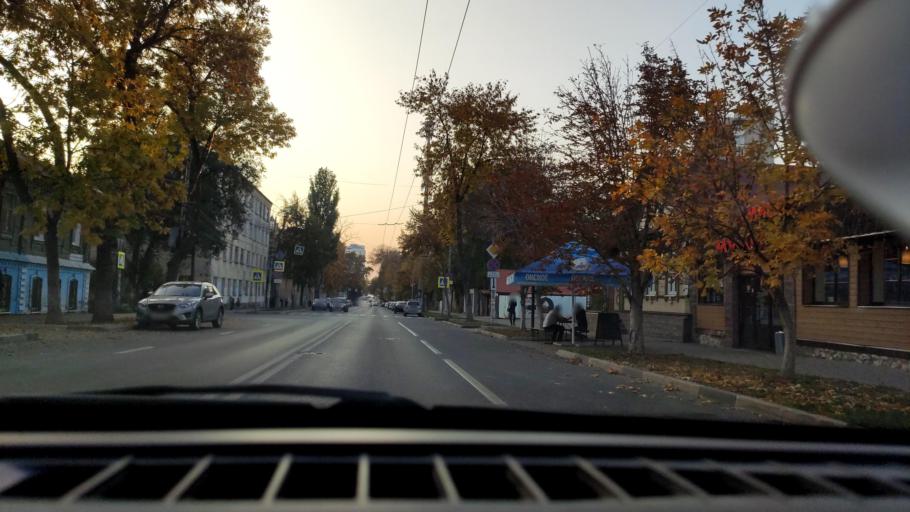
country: RU
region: Samara
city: Samara
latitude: 53.1971
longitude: 50.1169
